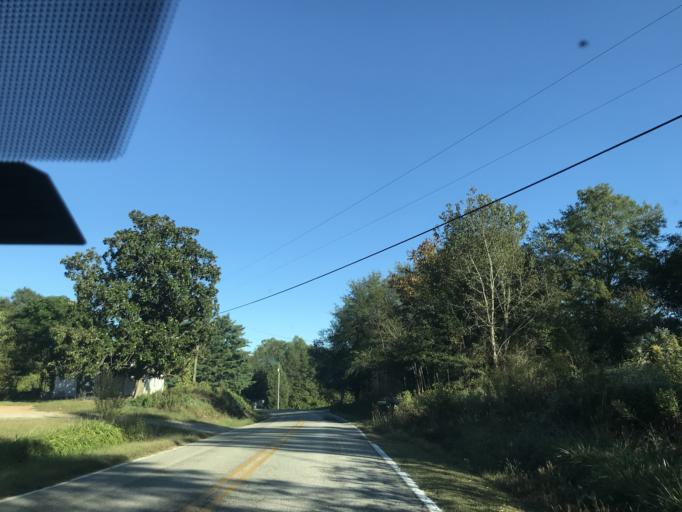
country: US
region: South Carolina
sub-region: Spartanburg County
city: Mayo
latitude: 35.1123
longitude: -81.8177
